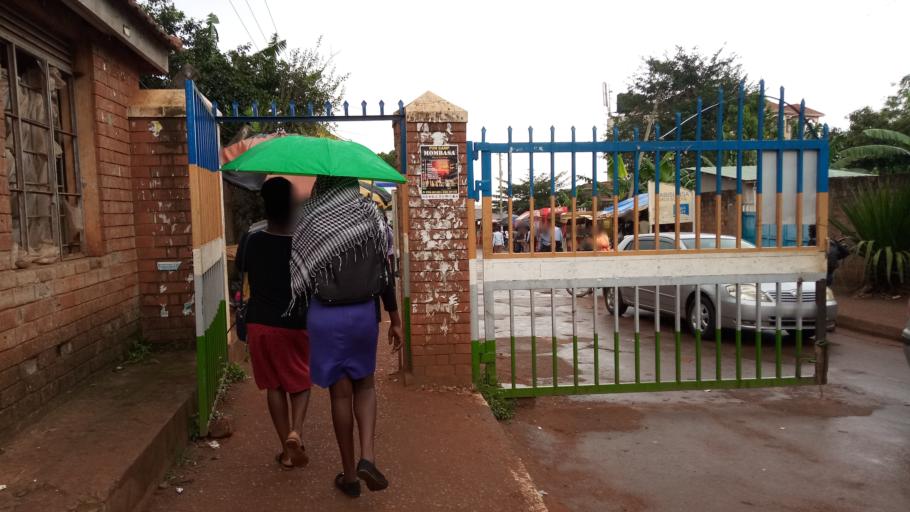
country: UG
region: Central Region
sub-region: Wakiso District
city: Kireka
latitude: 0.3457
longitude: 32.6341
